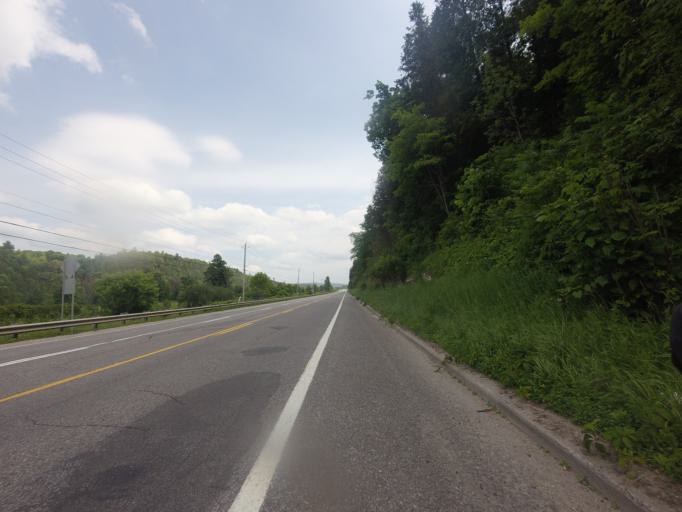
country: CA
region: Quebec
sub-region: Outaouais
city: Wakefield
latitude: 45.7575
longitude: -75.9190
